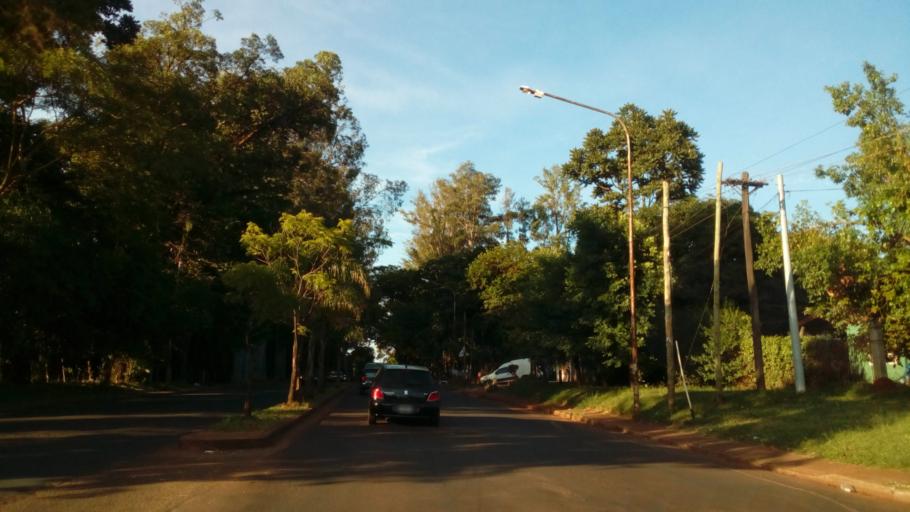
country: AR
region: Misiones
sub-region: Departamento de Capital
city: Posadas
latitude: -27.3956
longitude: -55.9205
